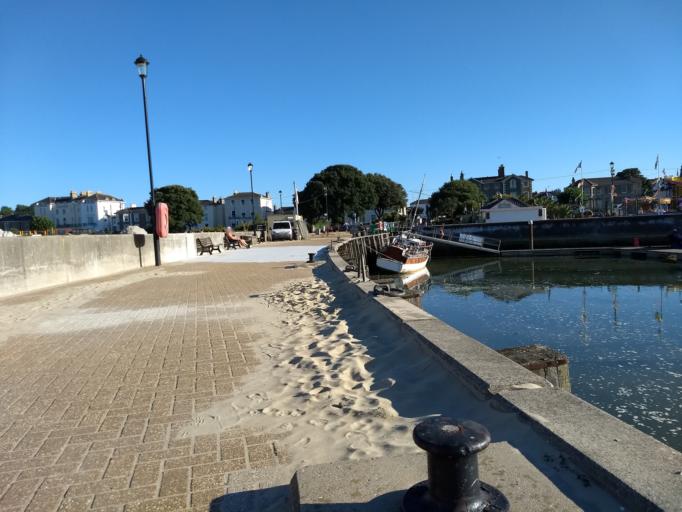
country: GB
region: England
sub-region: Isle of Wight
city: Ryde
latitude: 50.7322
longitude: -1.1533
